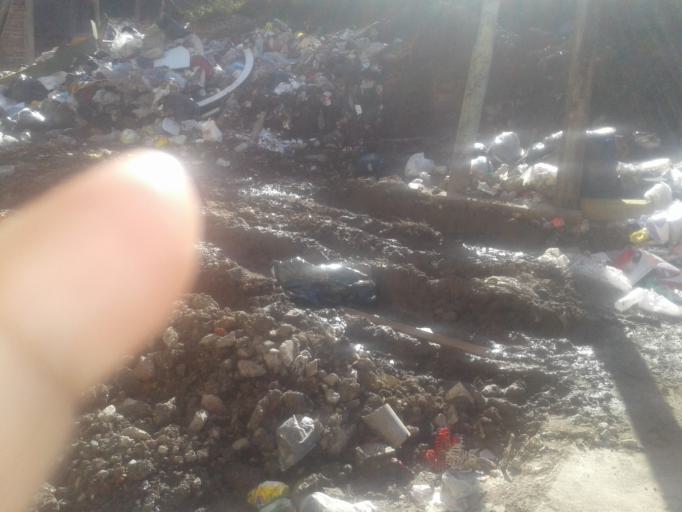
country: AR
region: Buenos Aires F.D.
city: Villa Lugano
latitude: -34.6713
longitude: -58.4621
